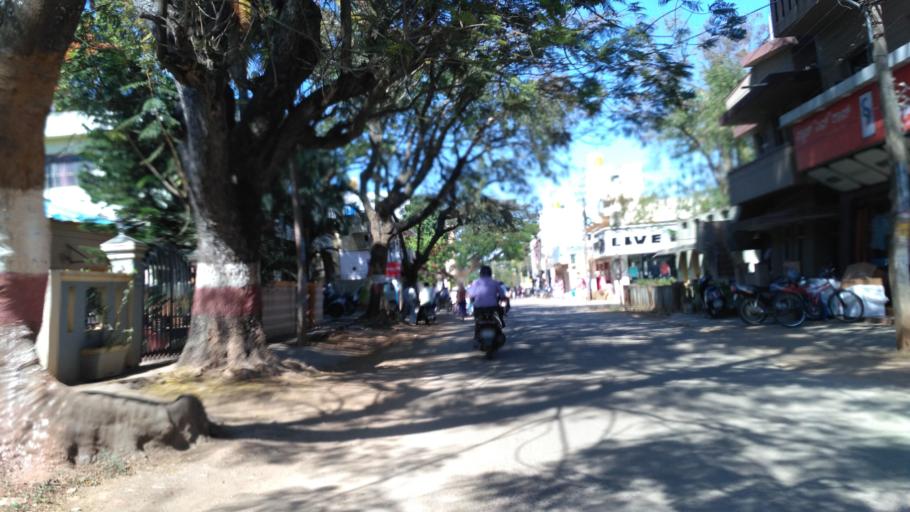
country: IN
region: Karnataka
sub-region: Hassan
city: Hassan
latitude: 13.0097
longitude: 76.1061
